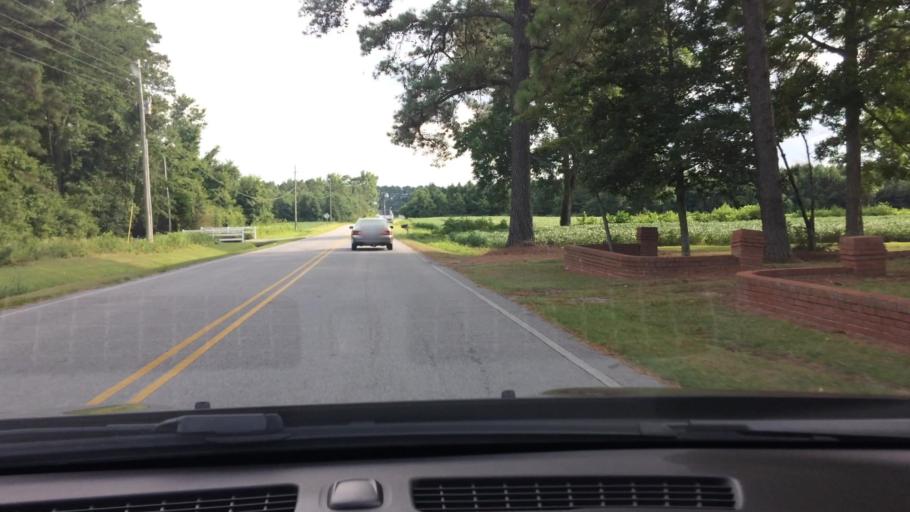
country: US
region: North Carolina
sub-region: Pitt County
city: Ayden
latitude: 35.4812
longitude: -77.3773
